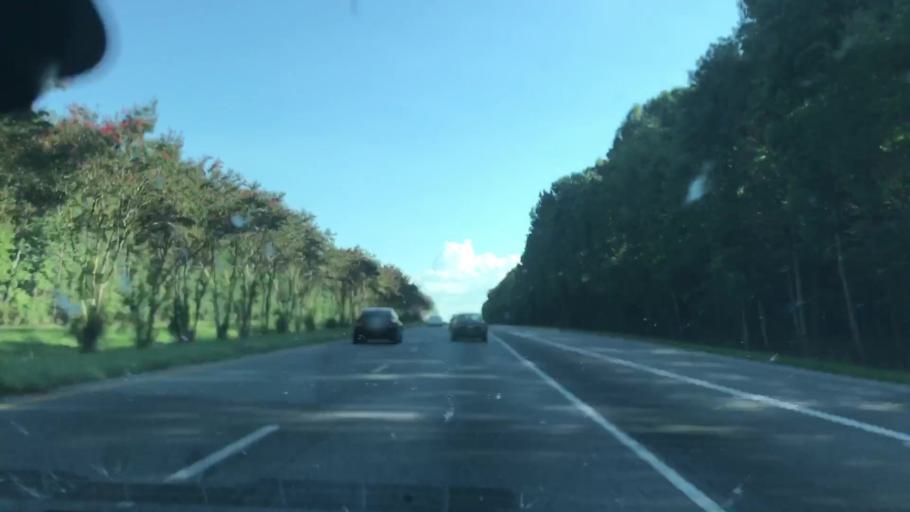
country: US
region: Georgia
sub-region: Harris County
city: Hamilton
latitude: 32.8104
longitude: -85.0214
